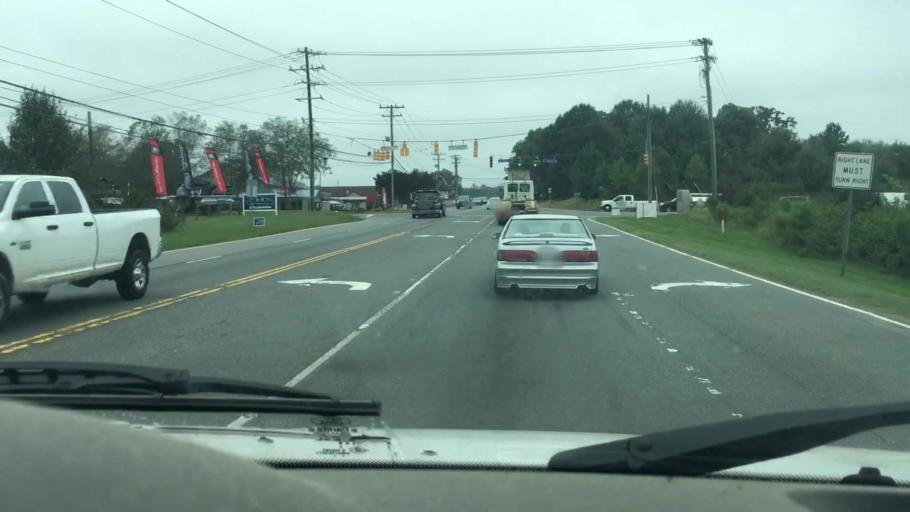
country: US
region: North Carolina
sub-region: Catawba County
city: Lake Norman of Catawba
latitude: 35.6014
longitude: -80.8962
